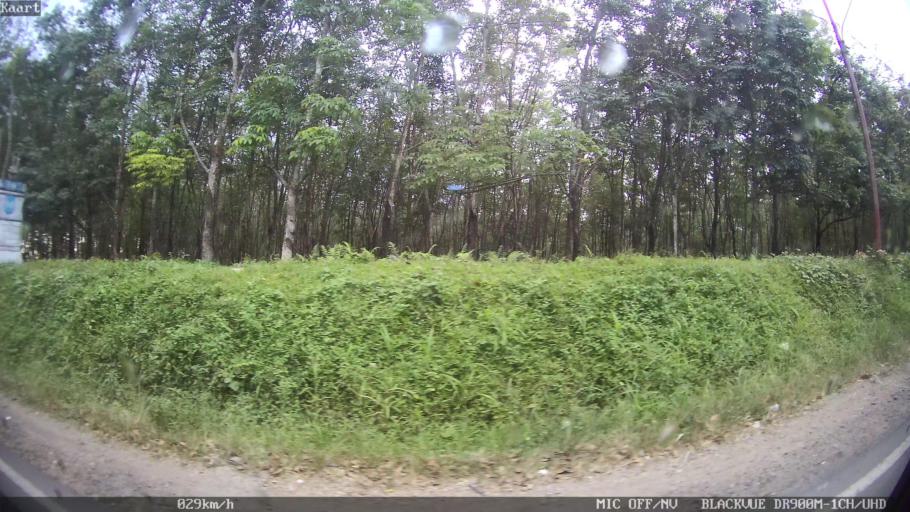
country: ID
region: Lampung
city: Gedongtataan
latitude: -5.3694
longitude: 105.1343
